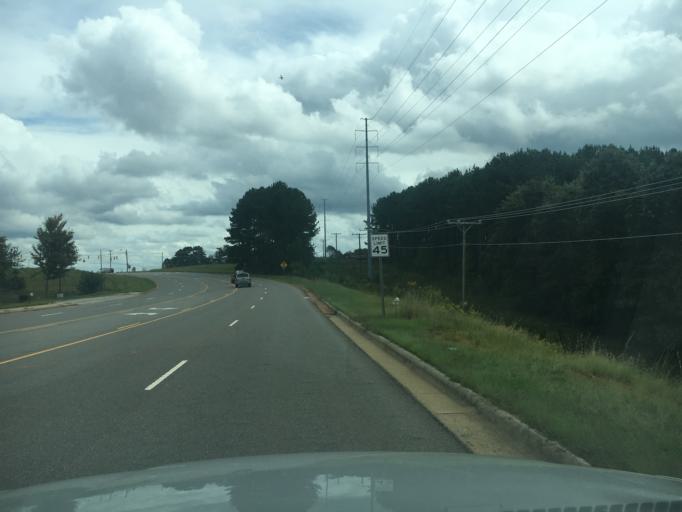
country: US
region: North Carolina
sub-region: Catawba County
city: Hickory
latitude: 35.6975
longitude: -81.2946
